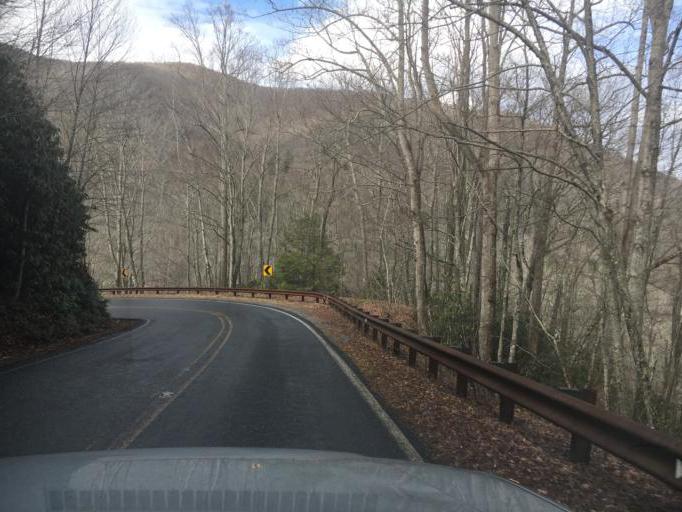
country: US
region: North Carolina
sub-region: Transylvania County
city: Brevard
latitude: 35.3678
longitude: -82.8141
